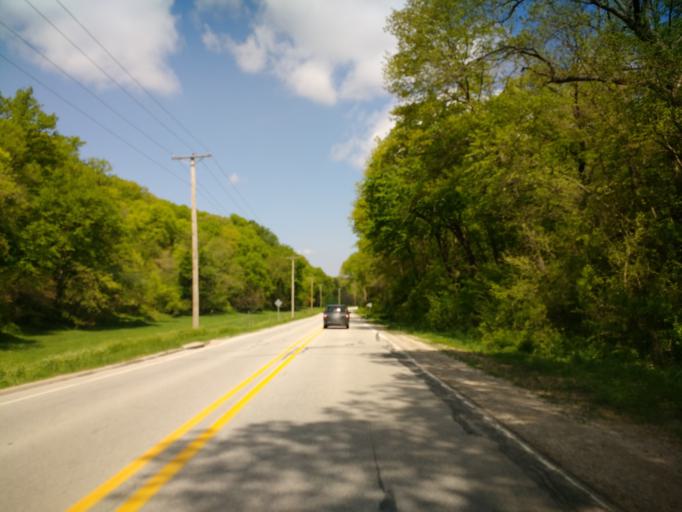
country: US
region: Iowa
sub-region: Harrison County
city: Missouri Valley
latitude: 41.4266
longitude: -95.8544
